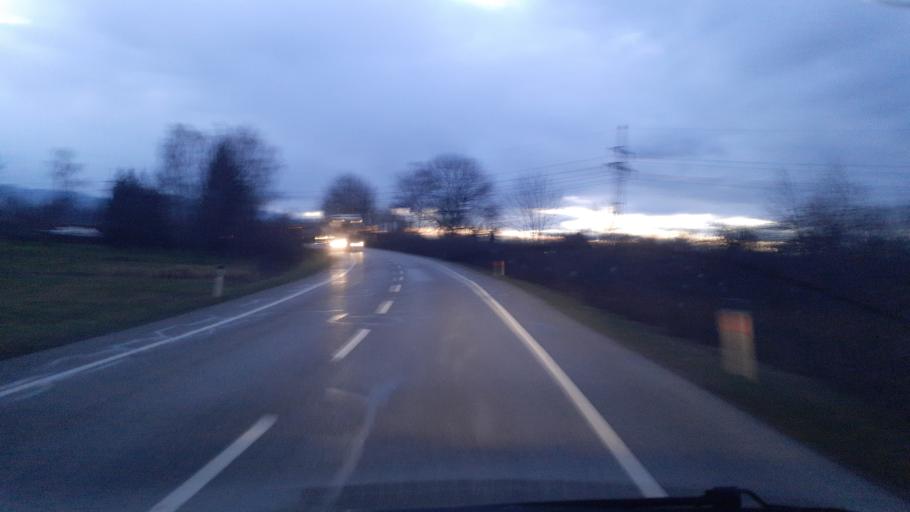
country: AT
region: Vorarlberg
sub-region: Politischer Bezirk Bregenz
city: Wolfurt
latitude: 47.4572
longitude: 9.7258
